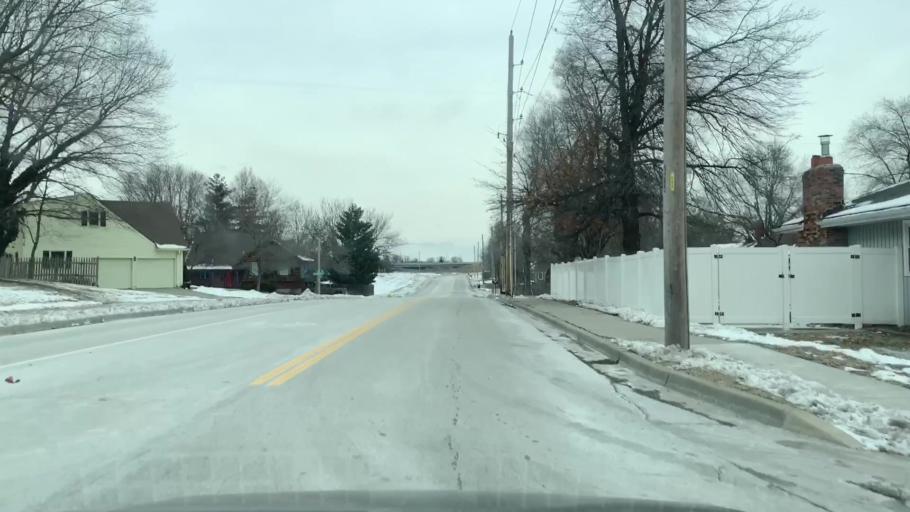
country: US
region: Missouri
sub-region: Jackson County
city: Lees Summit
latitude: 38.9415
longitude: -94.3643
